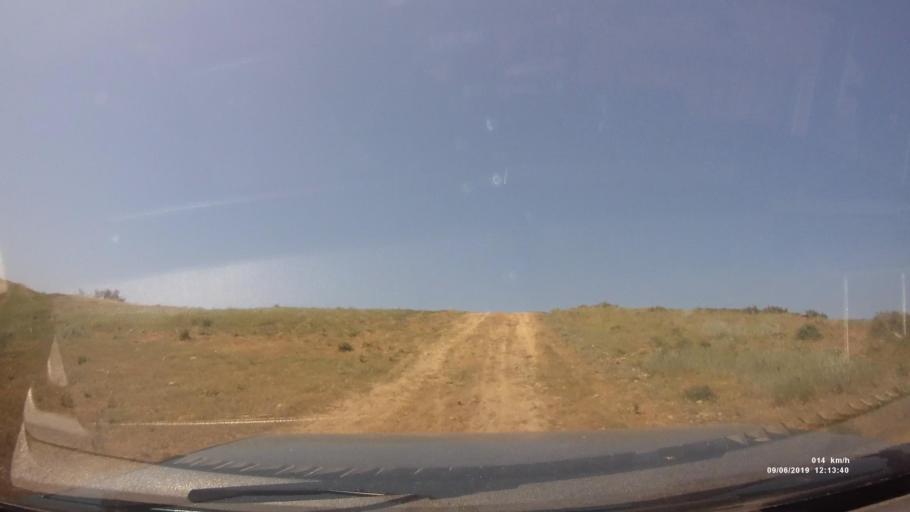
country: RU
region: Rostov
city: Staraya Stanitsa
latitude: 48.2509
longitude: 40.3268
